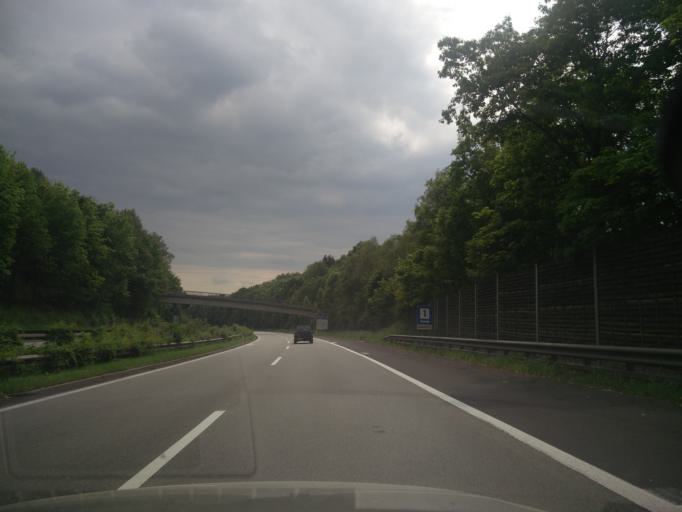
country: AT
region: Upper Austria
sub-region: Politischer Bezirk Urfahr-Umgebung
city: Altenberg bei Linz
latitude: 48.3362
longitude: 14.3312
